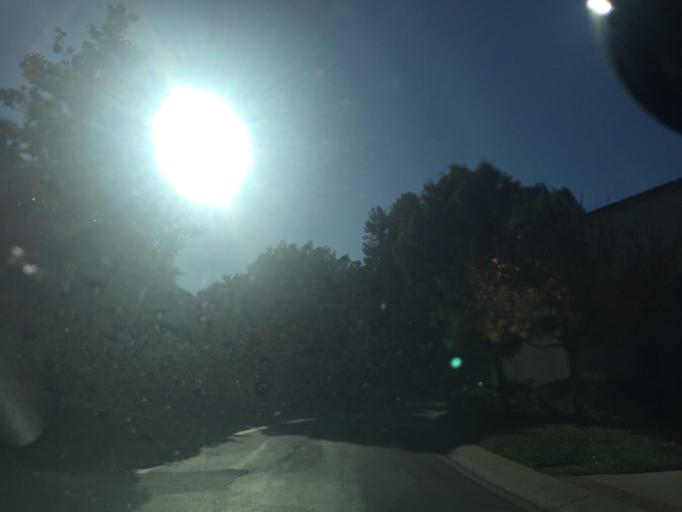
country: US
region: California
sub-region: San Diego County
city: Lemon Grove
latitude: 32.7735
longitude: -117.1013
